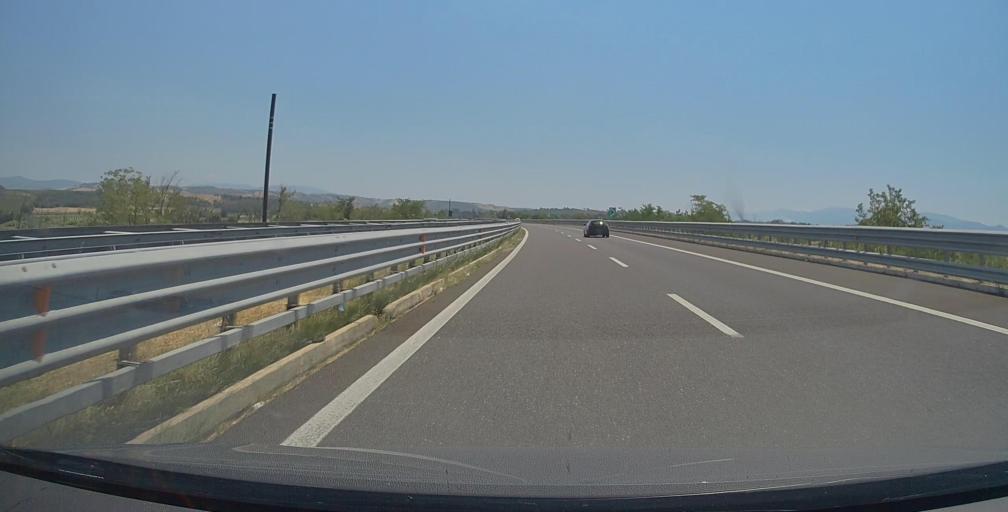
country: IT
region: Calabria
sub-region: Provincia di Cosenza
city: Roggiano Gravina
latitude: 39.6638
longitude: 16.2140
